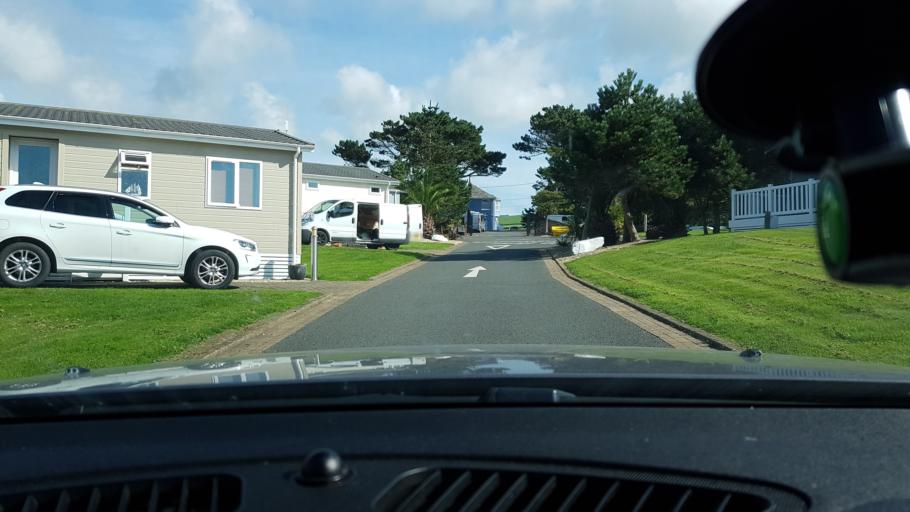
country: GB
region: England
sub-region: Cornwall
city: Tintagel
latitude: 50.6680
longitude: -4.7384
